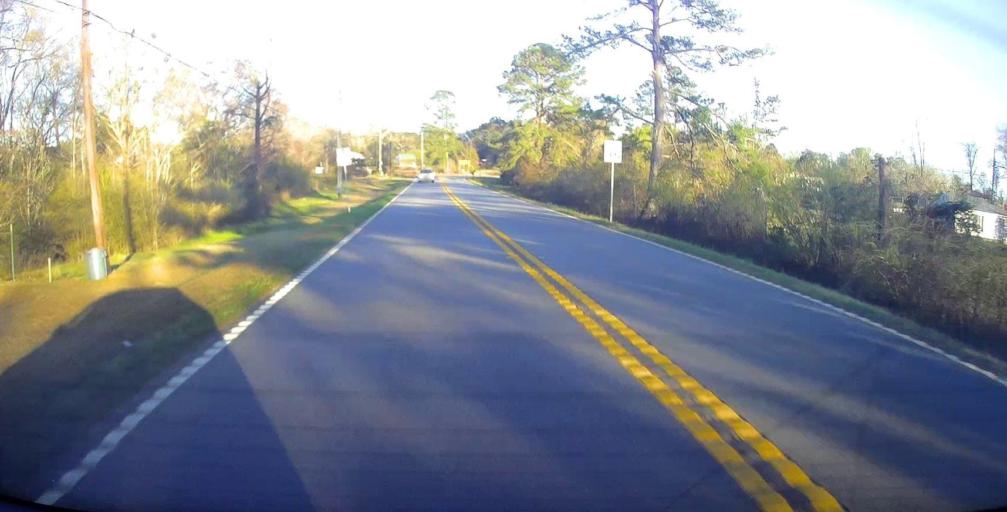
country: US
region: Georgia
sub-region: Harris County
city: Hamilton
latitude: 32.6231
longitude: -84.8165
